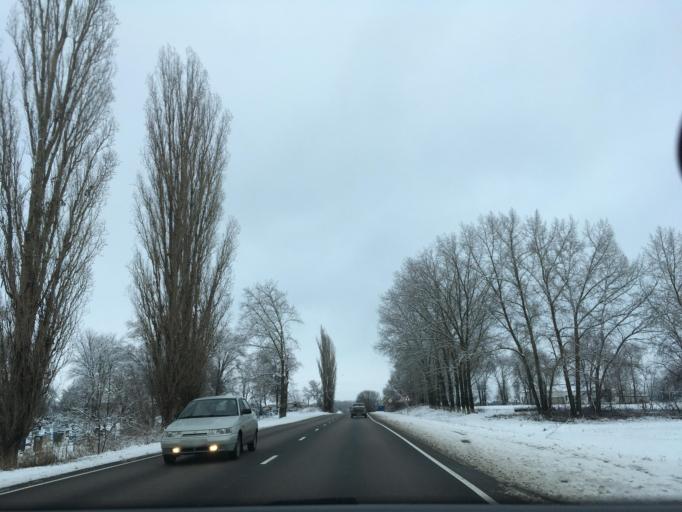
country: RU
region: Voronezj
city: Zabolotovka
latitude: 50.2466
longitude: 39.3670
